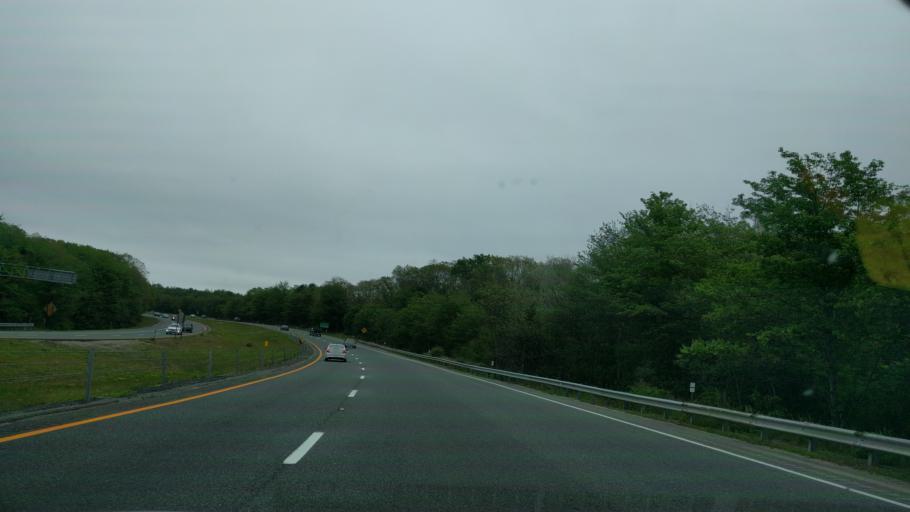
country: US
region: Rhode Island
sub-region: Newport County
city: Tiverton
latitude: 41.6412
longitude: -71.1842
